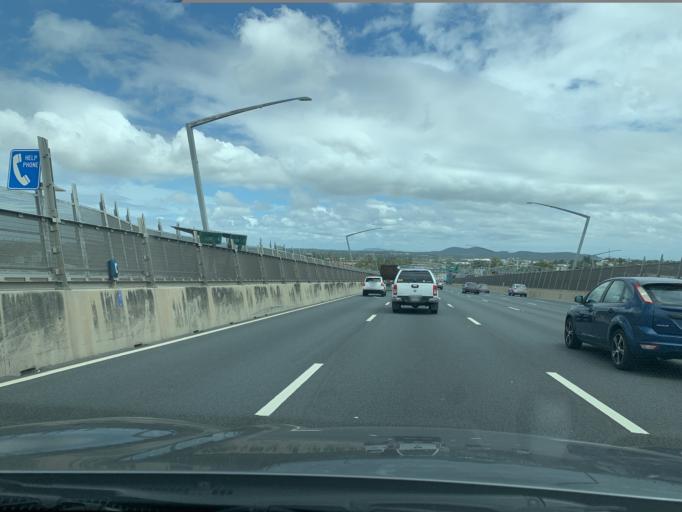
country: AU
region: Queensland
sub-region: Brisbane
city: Cannon Hill
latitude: -27.4482
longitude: 153.1035
